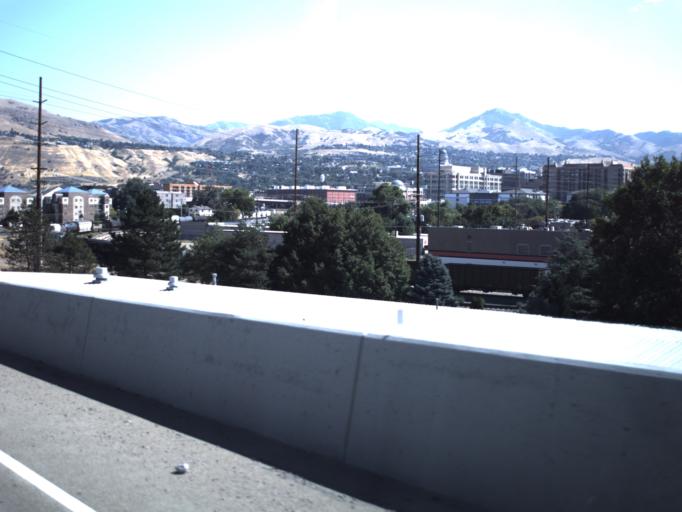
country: US
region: Utah
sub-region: Salt Lake County
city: Salt Lake City
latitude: 40.7662
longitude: -111.9124
